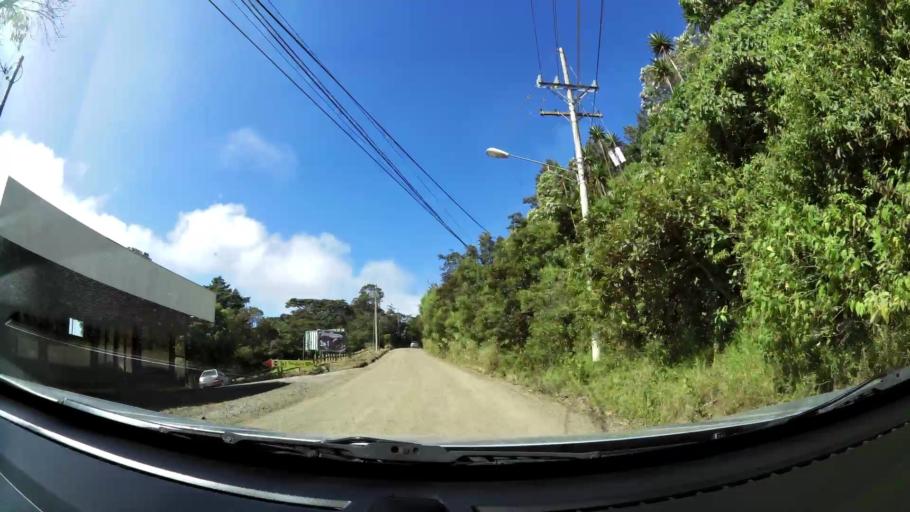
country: CR
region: Guanacaste
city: Juntas
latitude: 10.3265
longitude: -84.8348
